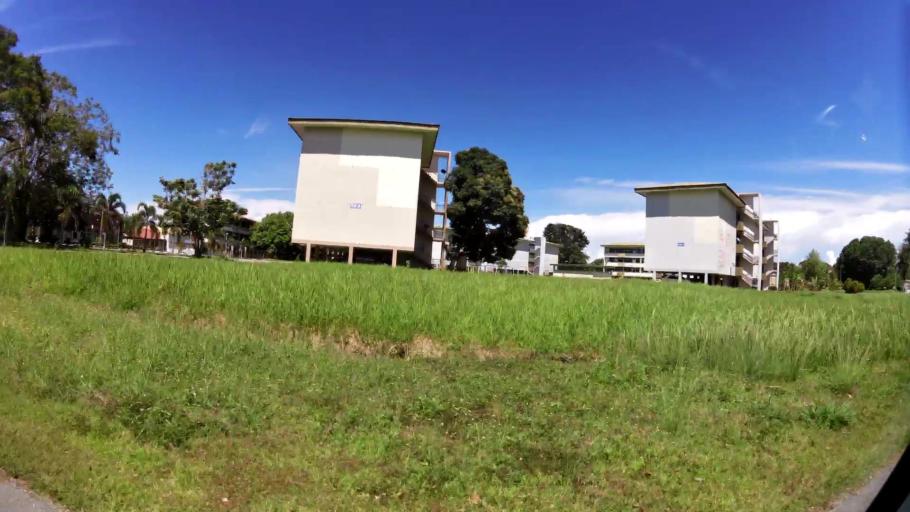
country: BN
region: Brunei and Muara
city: Bandar Seri Begawan
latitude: 5.0347
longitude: 115.0669
